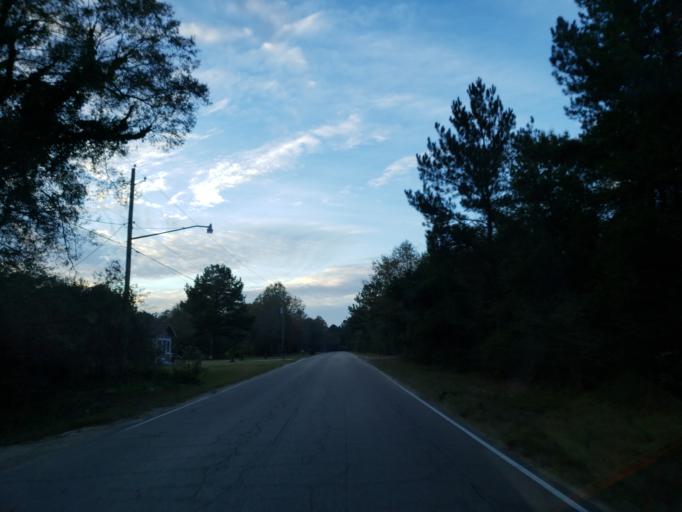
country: US
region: Mississippi
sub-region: Forrest County
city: Hattiesburg
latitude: 31.2803
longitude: -89.2496
